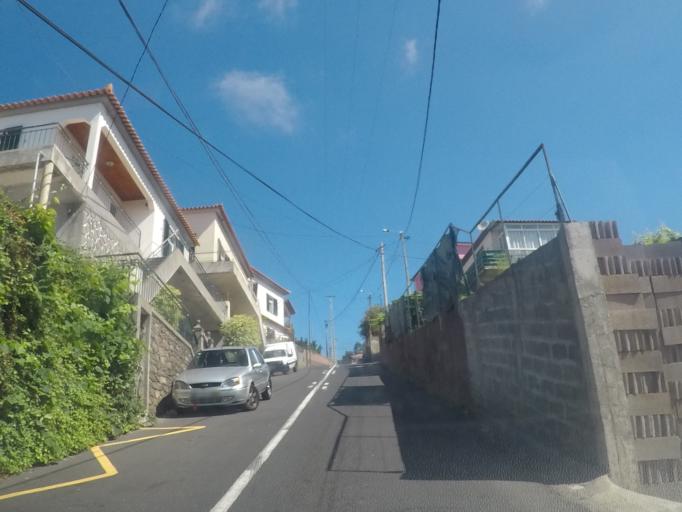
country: PT
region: Madeira
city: Camara de Lobos
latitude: 32.6744
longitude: -16.9646
